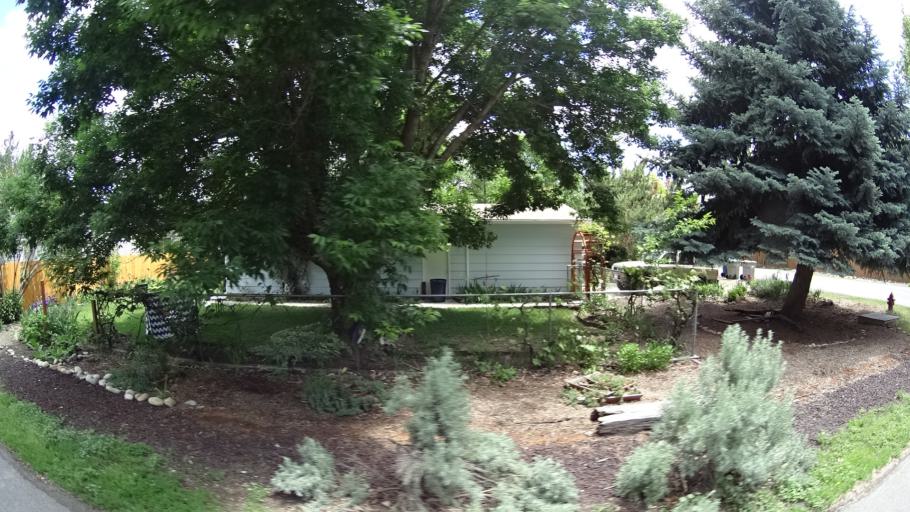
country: US
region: Idaho
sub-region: Ada County
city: Boise
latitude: 43.5858
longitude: -116.1986
